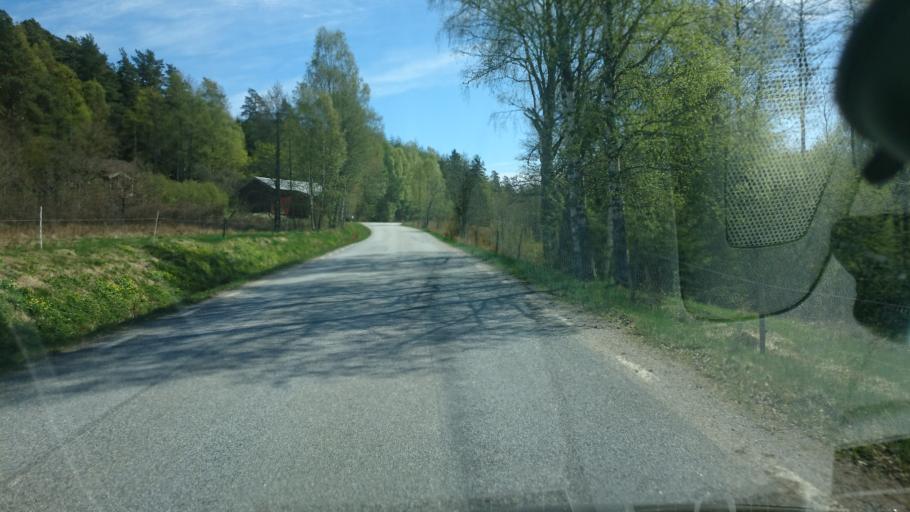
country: SE
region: Vaestra Goetaland
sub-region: Munkedals Kommun
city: Munkedal
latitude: 58.3734
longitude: 11.6855
